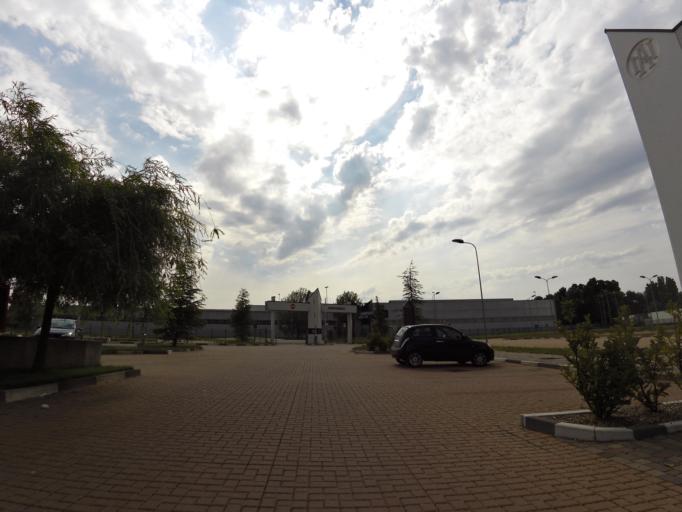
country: IT
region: Lombardy
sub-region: Citta metropolitana di Milano
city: Carpiano
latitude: 45.3488
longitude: 9.2819
